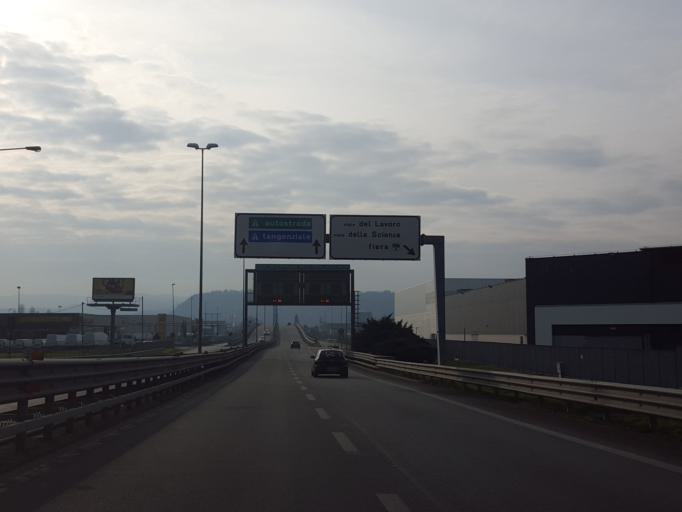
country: IT
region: Veneto
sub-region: Provincia di Vicenza
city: Creazzo
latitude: 45.5300
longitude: 11.5097
